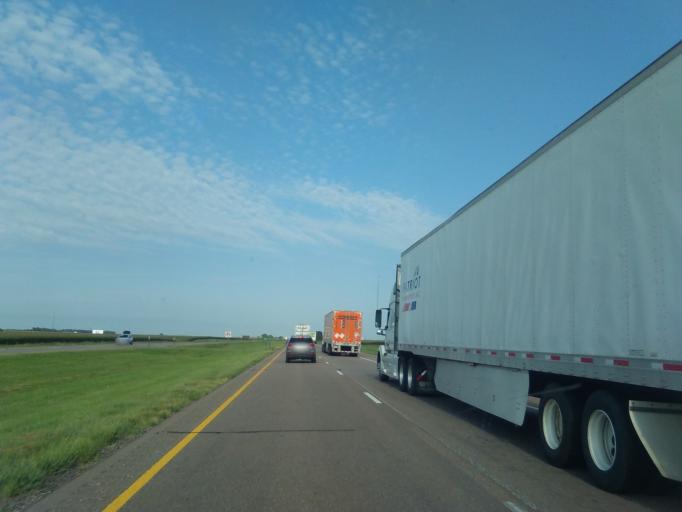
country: US
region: Nebraska
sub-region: York County
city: York
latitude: 40.8217
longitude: -97.7418
